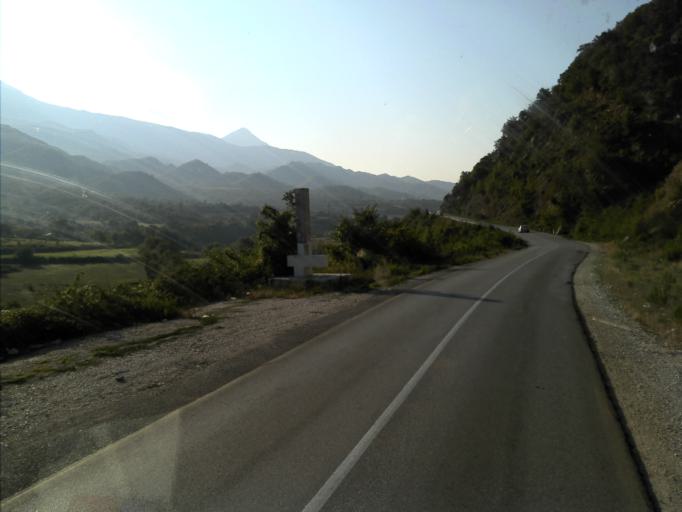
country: AL
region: Gjirokaster
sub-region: Rrethi i Gjirokastres
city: Picar
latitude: 40.2316
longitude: 20.0824
